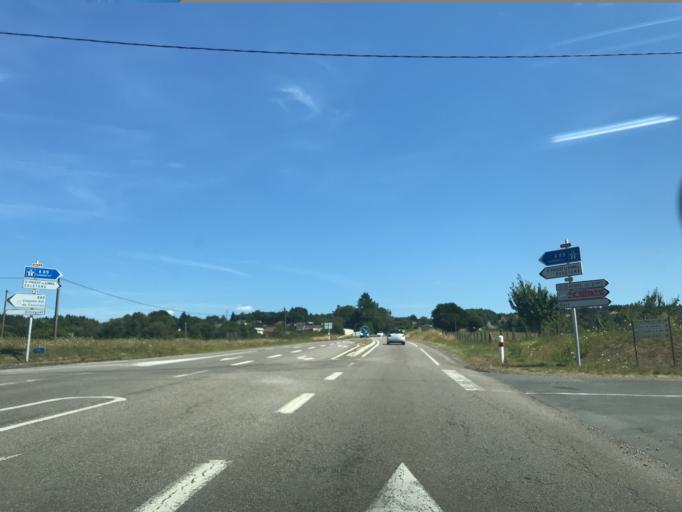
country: FR
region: Limousin
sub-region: Departement de la Correze
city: Naves
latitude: 45.3155
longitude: 1.8330
